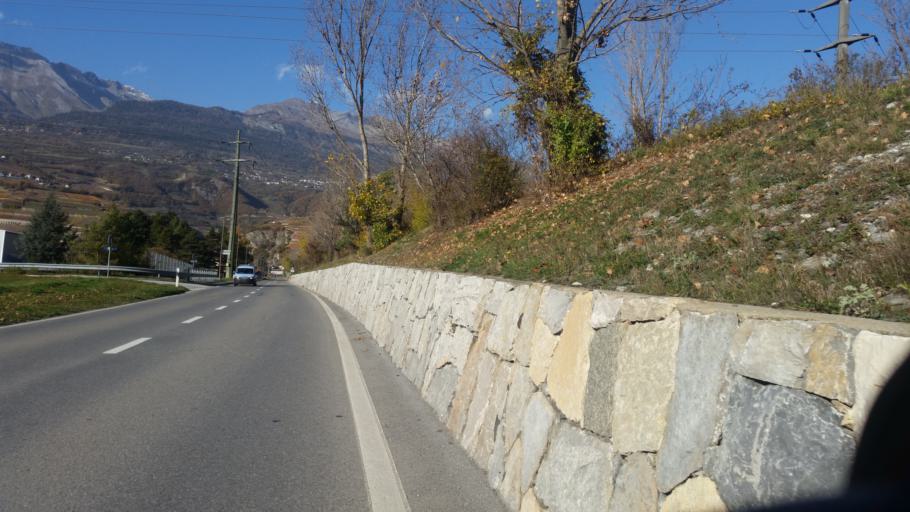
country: CH
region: Valais
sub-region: Sion District
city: Saint-Leonard
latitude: 46.2452
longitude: 7.4207
